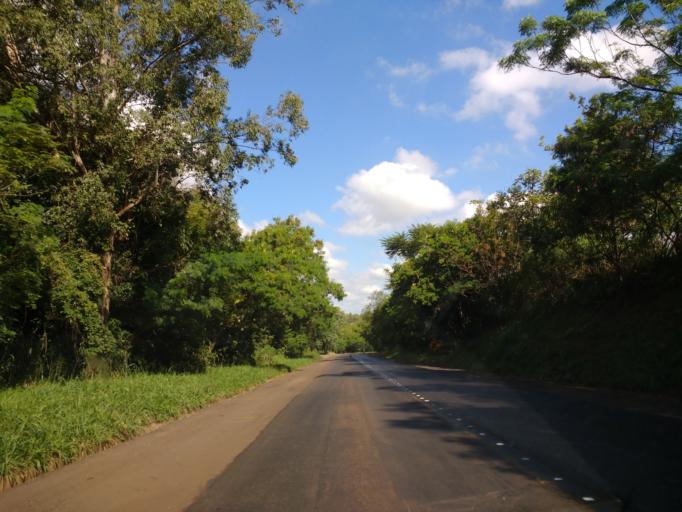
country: BR
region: Parana
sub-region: Umuarama
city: Umuarama
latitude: -23.8761
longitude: -53.3952
